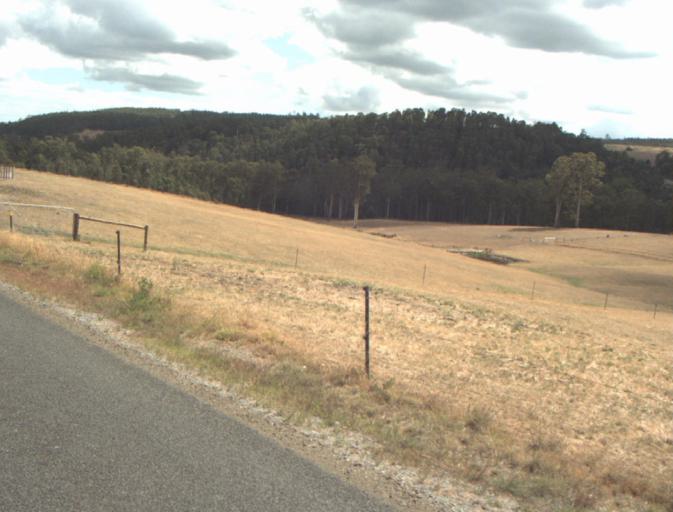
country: AU
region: Tasmania
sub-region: Launceston
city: Mayfield
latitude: -41.2146
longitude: 147.1353
